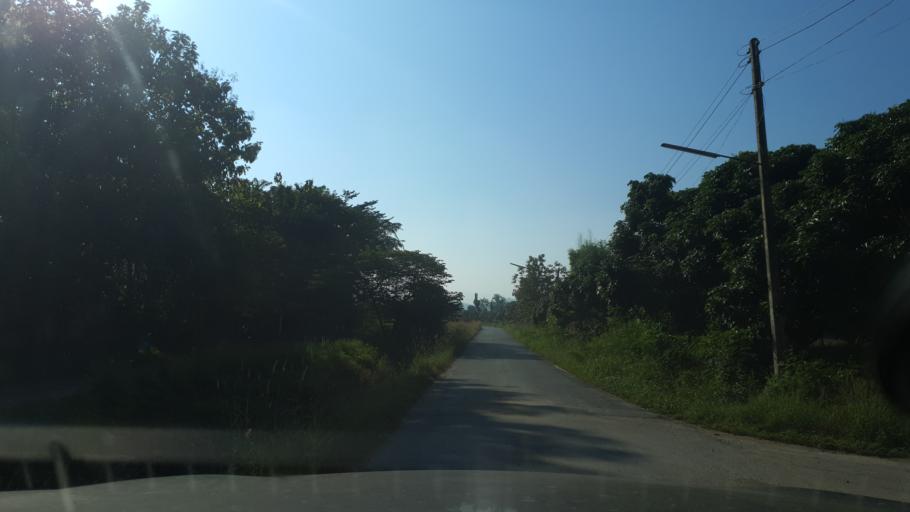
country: TH
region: Chiang Mai
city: San Kamphaeng
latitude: 18.7013
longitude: 99.1451
